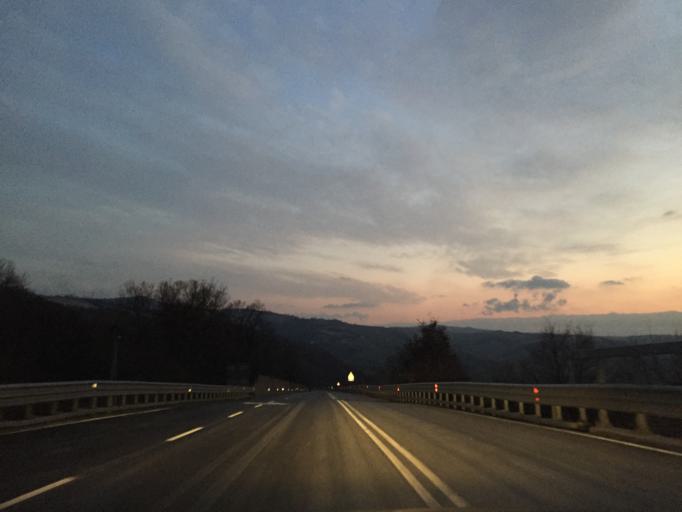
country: IT
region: Apulia
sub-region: Provincia di Foggia
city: Volturino
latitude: 41.4670
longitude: 15.0944
